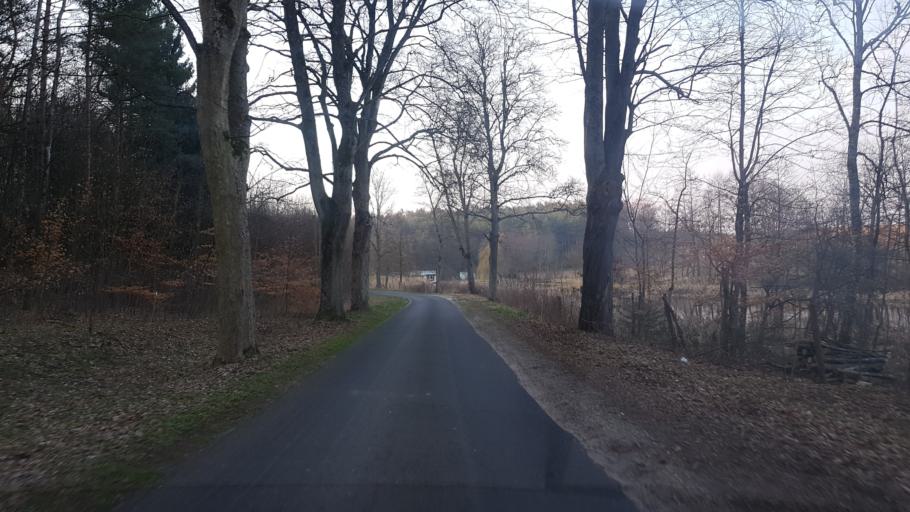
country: PL
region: West Pomeranian Voivodeship
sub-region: Powiat swidwinski
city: Swidwin
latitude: 53.7315
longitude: 15.7270
